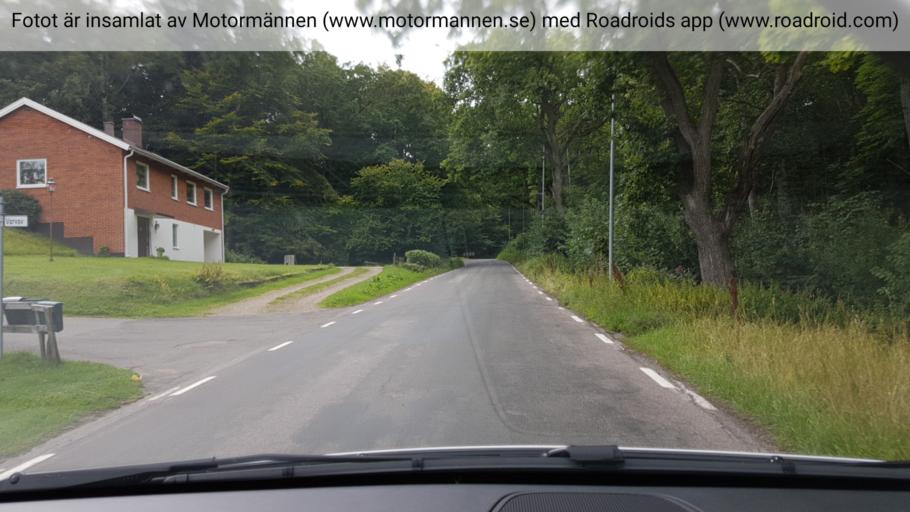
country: SE
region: Vaestra Goetaland
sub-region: Tidaholms Kommun
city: Tidaholm
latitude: 58.1967
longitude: 13.8404
